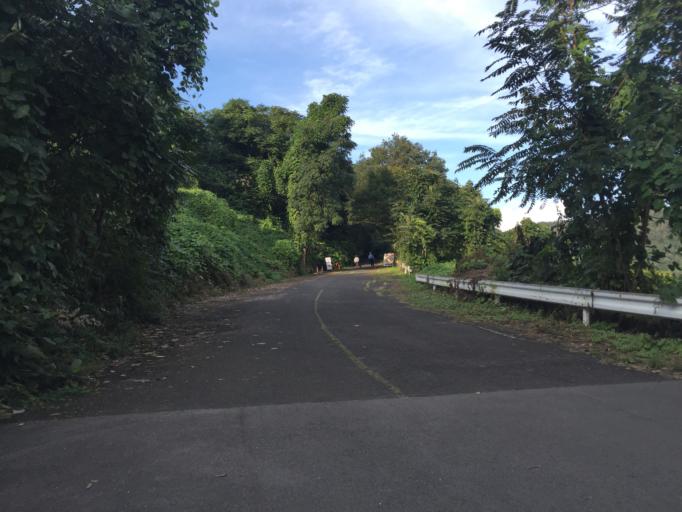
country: JP
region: Fukushima
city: Yanagawamachi-saiwaicho
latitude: 37.8903
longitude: 140.5460
